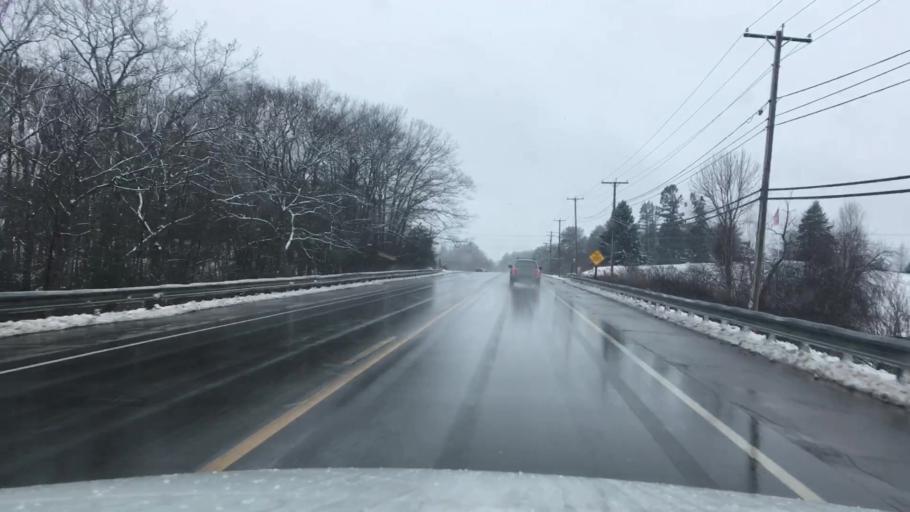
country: US
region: Maine
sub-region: Knox County
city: Warren
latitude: 44.1214
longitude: -69.2504
